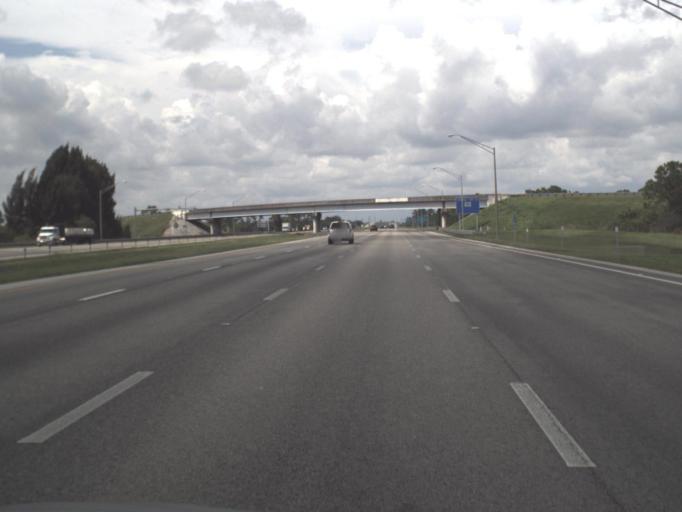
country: US
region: Florida
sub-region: Charlotte County
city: Charlotte Park
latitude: 26.8834
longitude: -81.9894
